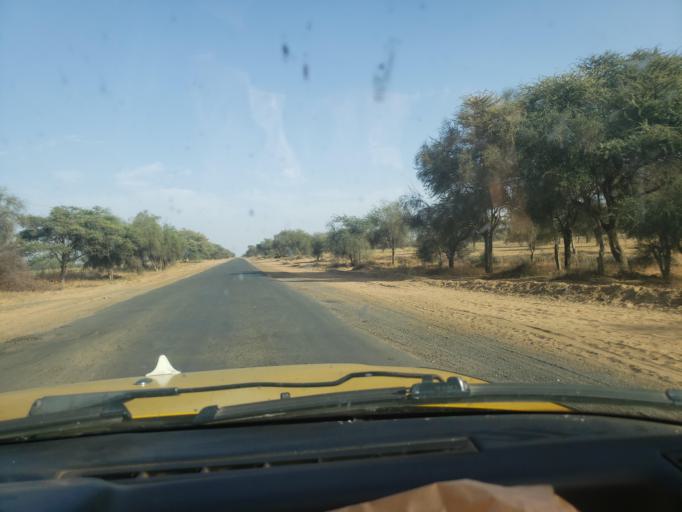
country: SN
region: Louga
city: Louga
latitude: 15.5051
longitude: -15.9579
